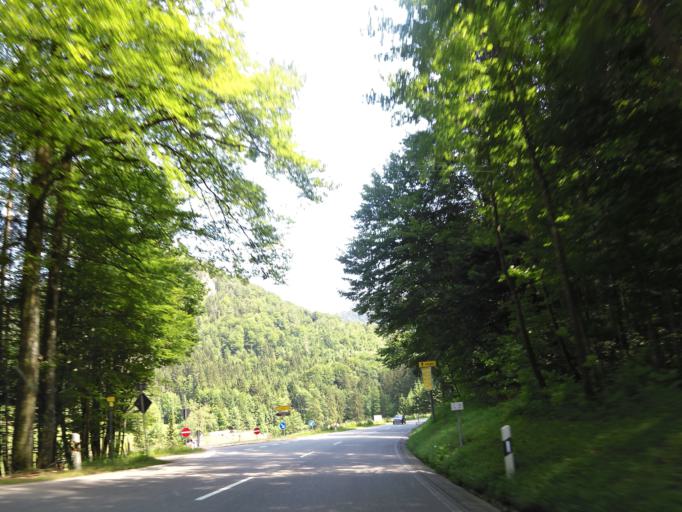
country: DE
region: Bavaria
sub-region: Upper Bavaria
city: Inzell
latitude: 47.7497
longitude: 12.7258
